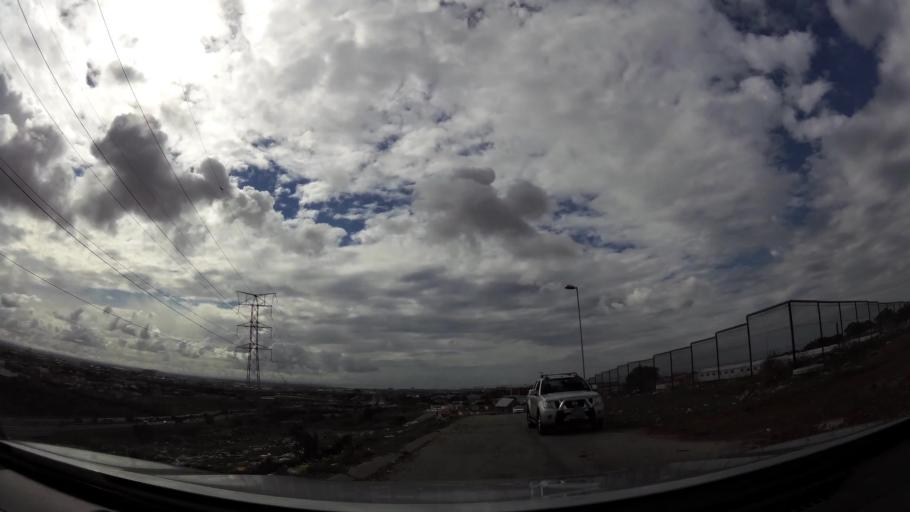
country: ZA
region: Eastern Cape
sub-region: Nelson Mandela Bay Metropolitan Municipality
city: Port Elizabeth
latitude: -33.9286
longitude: 25.5604
